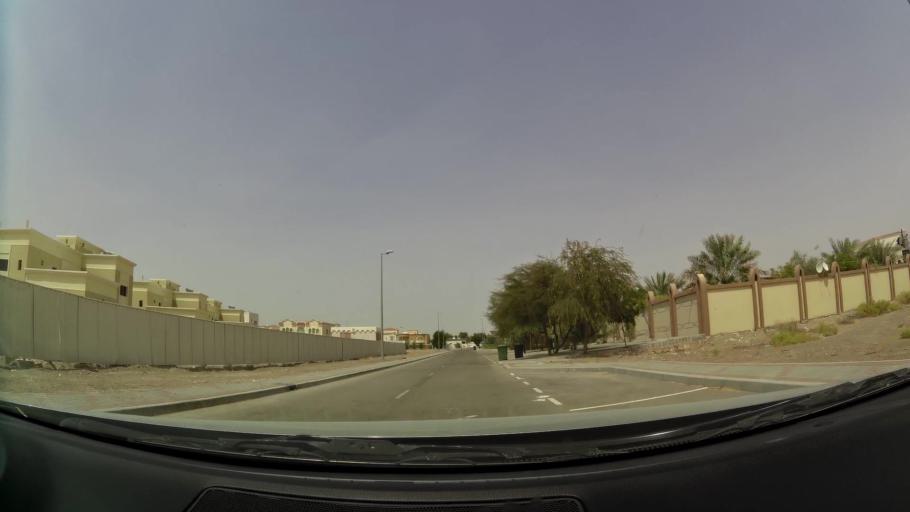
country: AE
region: Abu Dhabi
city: Al Ain
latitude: 24.1427
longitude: 55.6317
